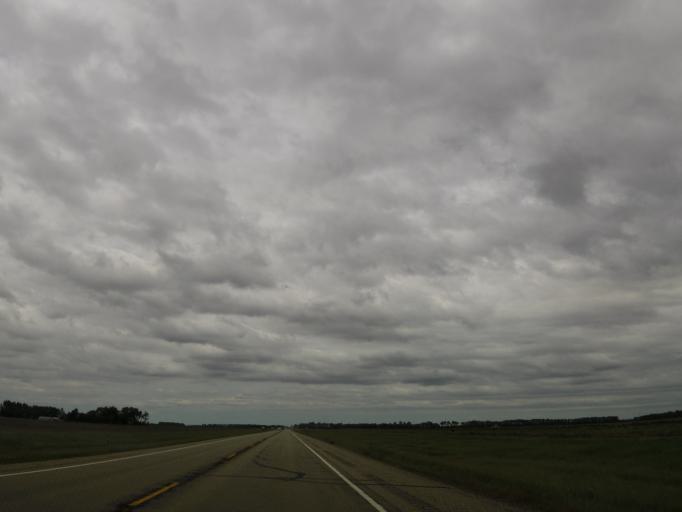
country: US
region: North Dakota
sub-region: Walsh County
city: Grafton
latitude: 48.5657
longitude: -97.4479
